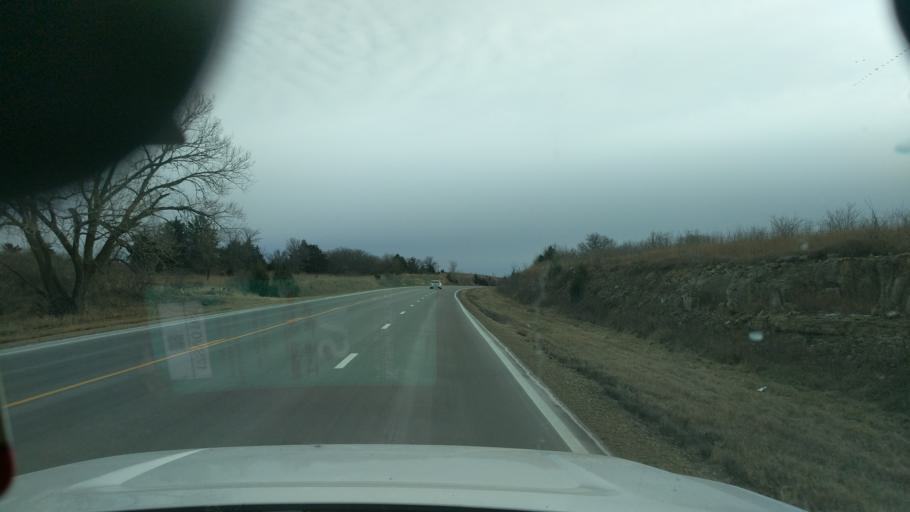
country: US
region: Kansas
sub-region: Geary County
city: Junction City
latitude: 38.9416
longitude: -96.8544
